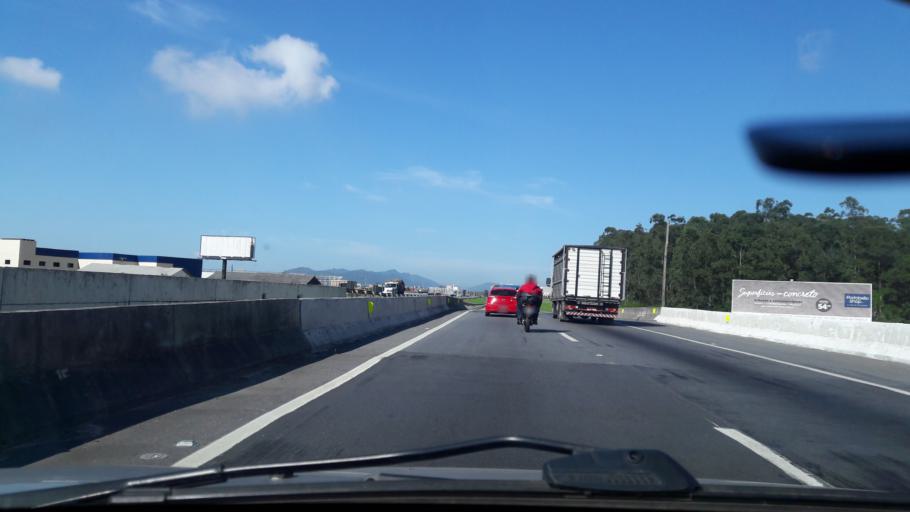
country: BR
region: Santa Catarina
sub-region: Tijucas
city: Tijucas
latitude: -27.2110
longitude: -48.6212
